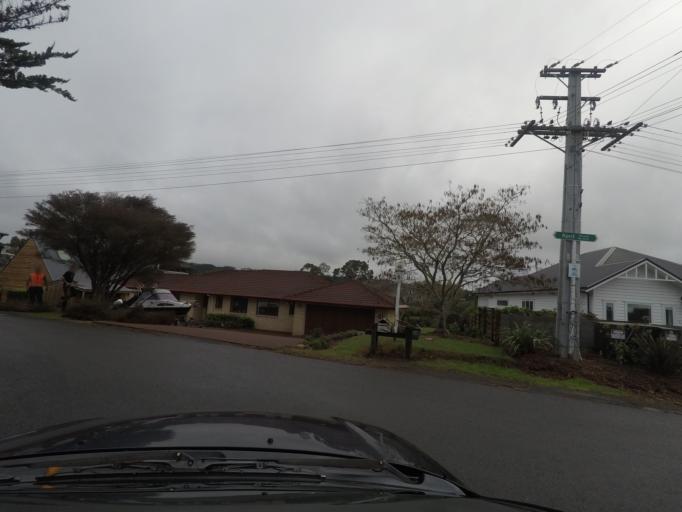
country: NZ
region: Auckland
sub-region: Auckland
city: Rosebank
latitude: -36.7615
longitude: 174.5974
